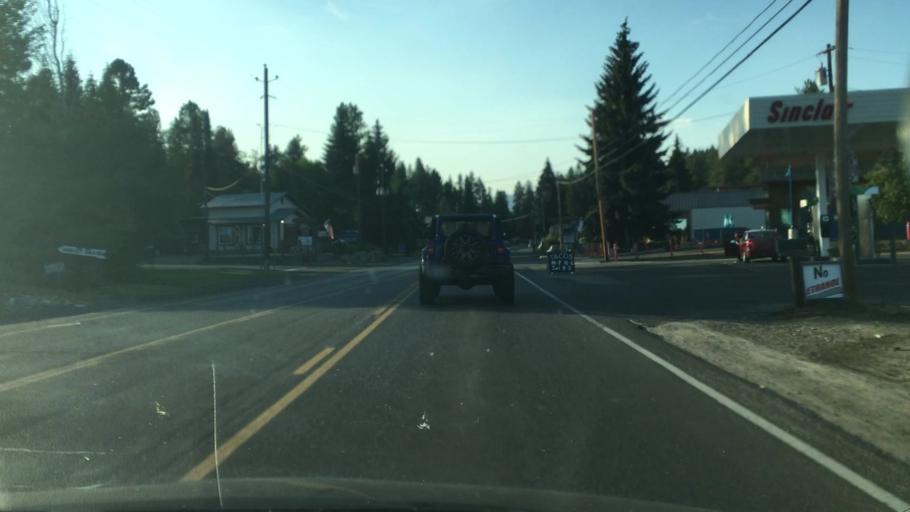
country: US
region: Idaho
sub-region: Valley County
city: McCall
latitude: 44.8989
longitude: -116.0970
